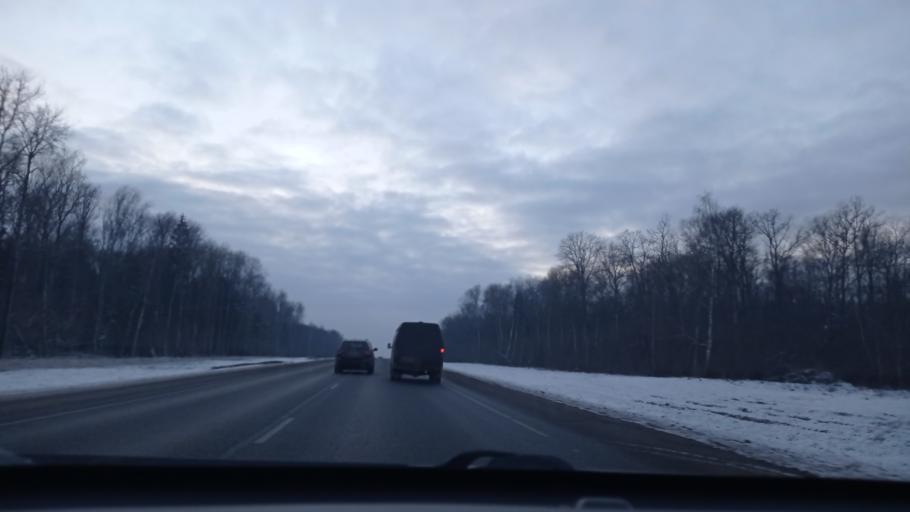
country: RU
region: Kaluga
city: Belousovo
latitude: 55.1326
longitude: 36.7683
